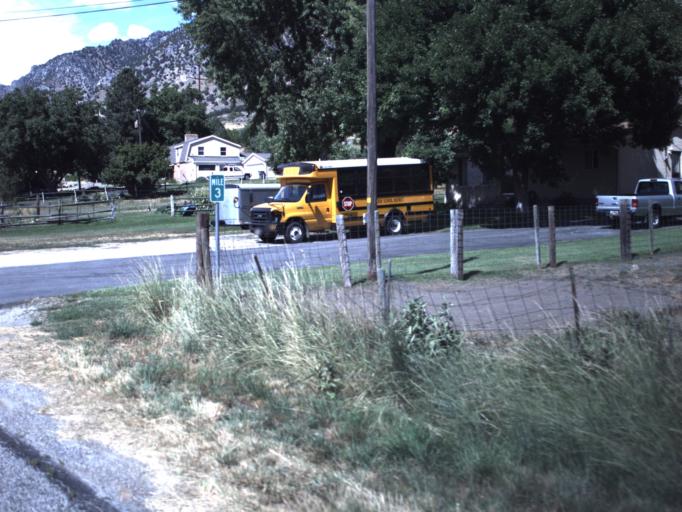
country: US
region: Utah
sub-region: Box Elder County
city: Brigham City
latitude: 41.5695
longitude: -112.0285
